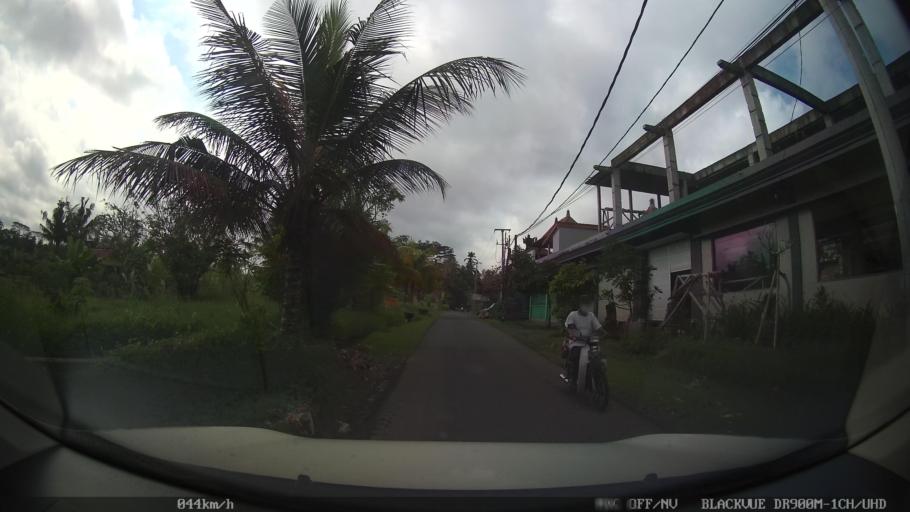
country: ID
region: Bali
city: Banjar Pesalakan
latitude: -8.4979
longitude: 115.3048
